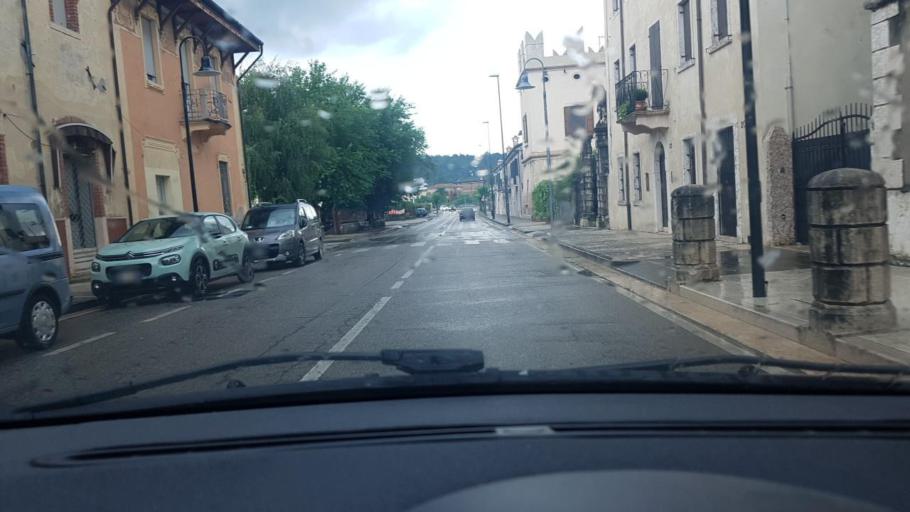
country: IT
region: Veneto
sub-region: Provincia di Verona
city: Caprino Veronese
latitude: 45.6044
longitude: 10.7947
